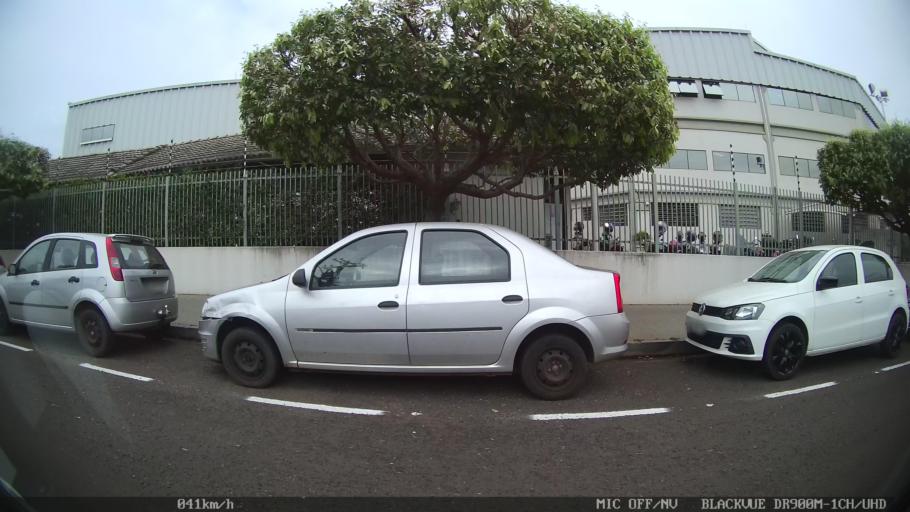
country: BR
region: Sao Paulo
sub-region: Sao Jose Do Rio Preto
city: Sao Jose do Rio Preto
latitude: -20.8280
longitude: -49.4197
